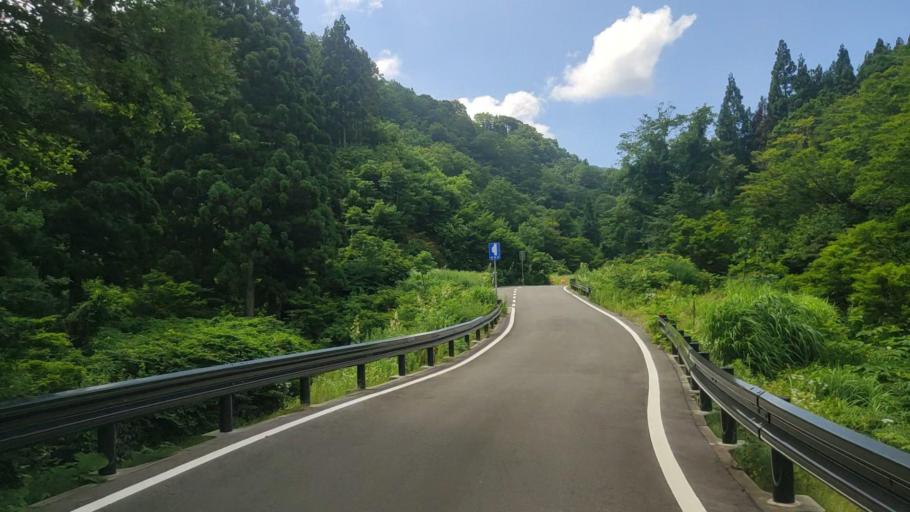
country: JP
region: Fukui
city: Katsuyama
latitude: 36.1619
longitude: 136.5266
